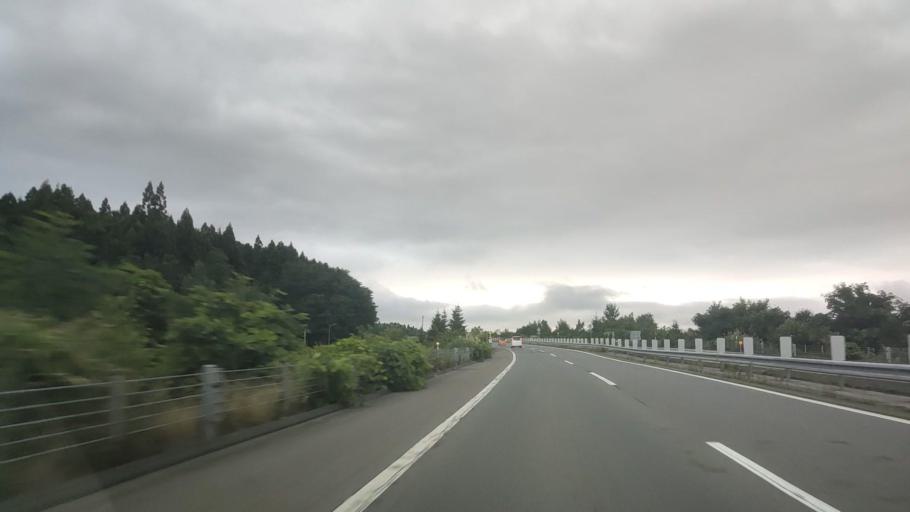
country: JP
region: Hokkaido
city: Nanae
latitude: 41.9049
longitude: 140.6979
